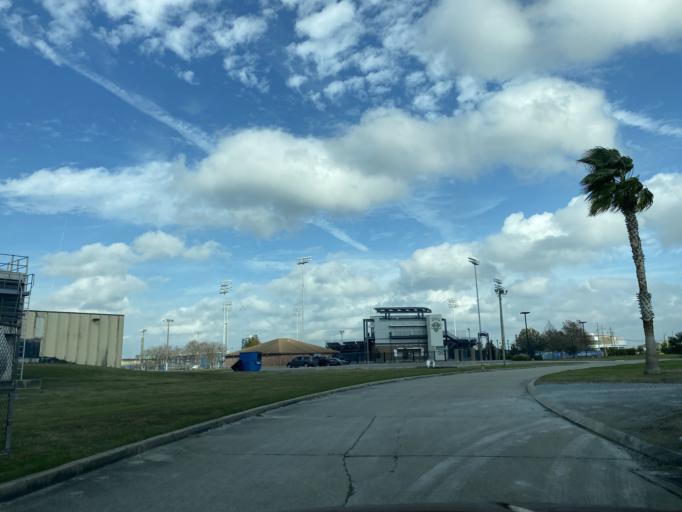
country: US
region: Louisiana
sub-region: Orleans Parish
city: New Orleans
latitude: 30.0294
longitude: -90.0487
